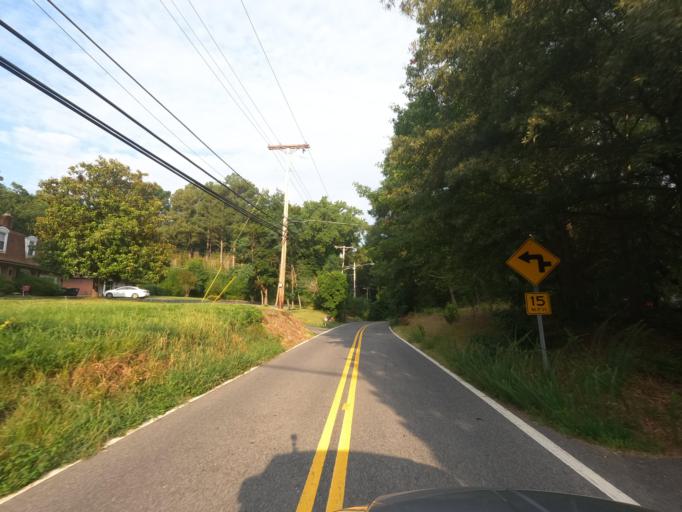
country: US
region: Maryland
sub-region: Prince George's County
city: Fort Washington
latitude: 38.6868
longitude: -77.0074
